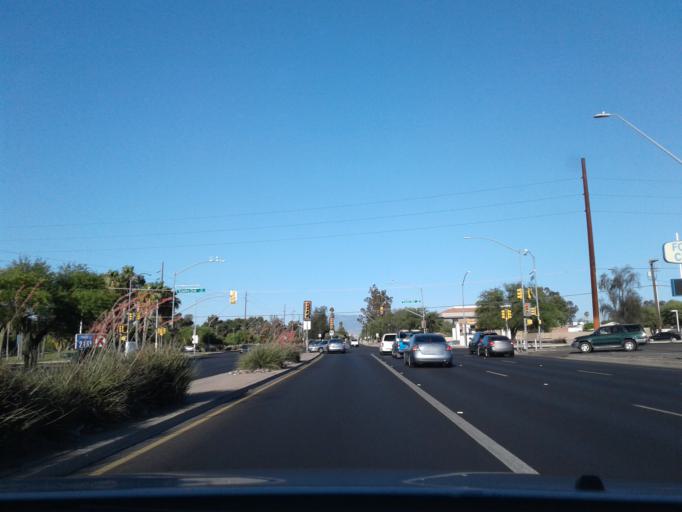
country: US
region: Arizona
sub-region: Pima County
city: Tucson
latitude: 32.2069
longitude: -110.9276
